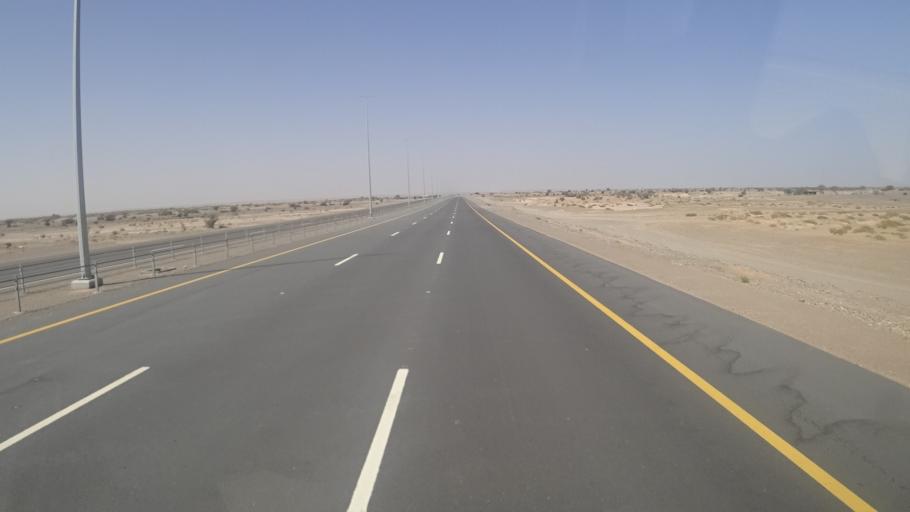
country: OM
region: Ash Sharqiyah
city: Badiyah
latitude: 22.2760
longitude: 59.1963
